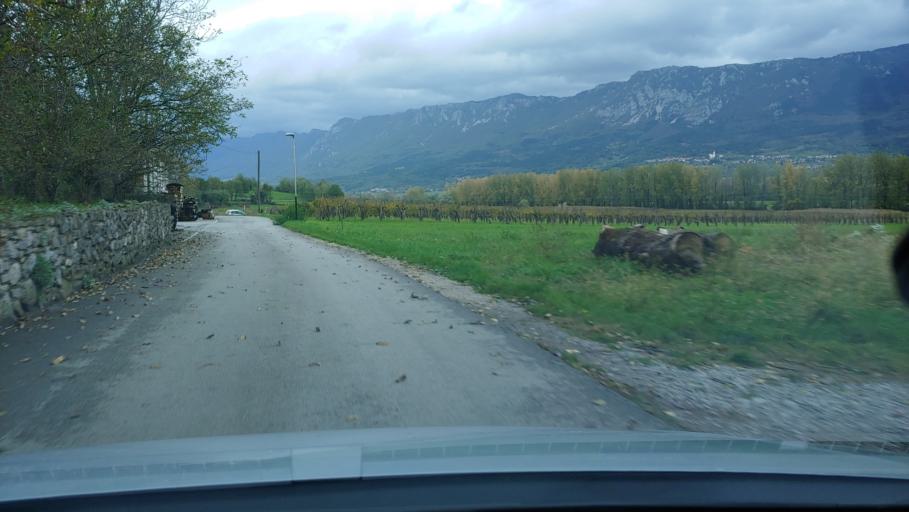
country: SI
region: Vipava
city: Vipava
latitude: 45.8414
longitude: 13.9392
